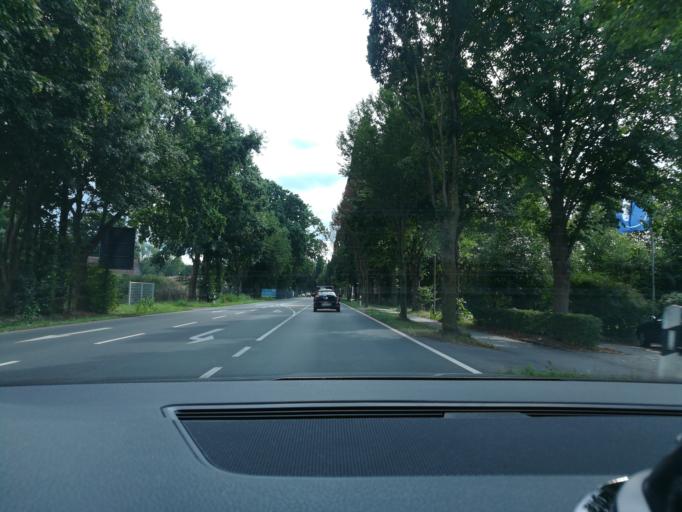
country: DE
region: North Rhine-Westphalia
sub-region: Regierungsbezirk Detmold
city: Minden
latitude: 52.3164
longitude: 8.8800
